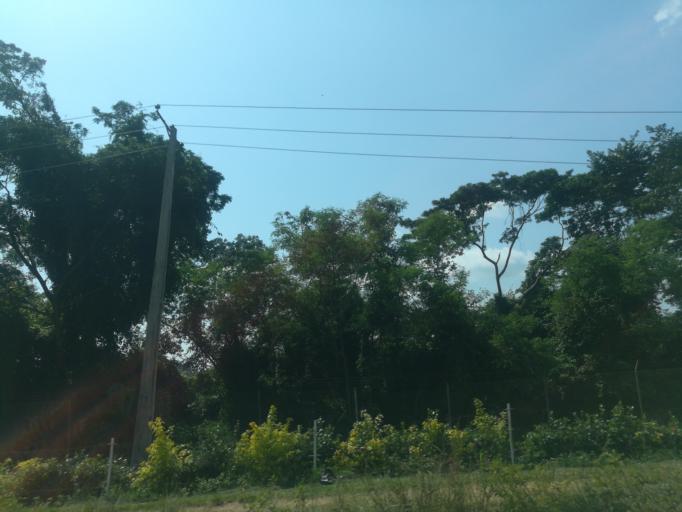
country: NG
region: Oyo
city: Moniya
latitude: 7.5035
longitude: 3.9131
